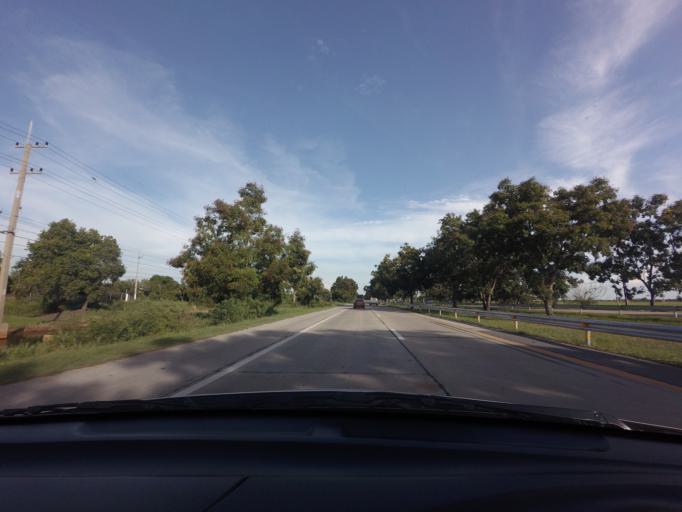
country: TH
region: Phra Nakhon Si Ayutthaya
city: Lat Bua Luang
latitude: 14.2083
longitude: 100.2878
